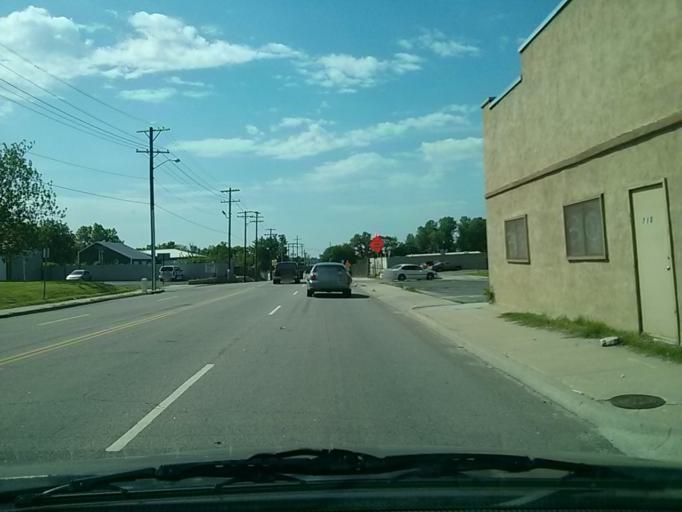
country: US
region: Oklahoma
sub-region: Tulsa County
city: Tulsa
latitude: 36.1648
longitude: -95.9756
